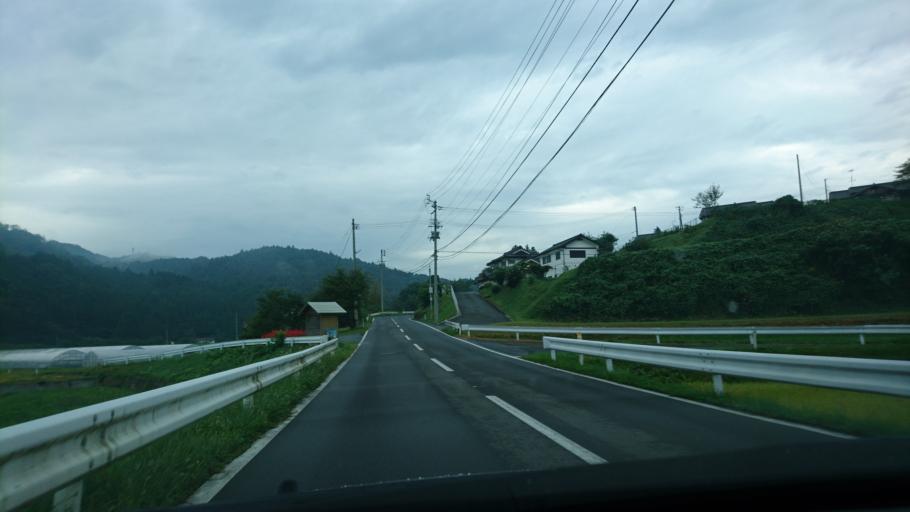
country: JP
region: Iwate
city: Ichinoseki
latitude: 38.9496
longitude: 141.2528
